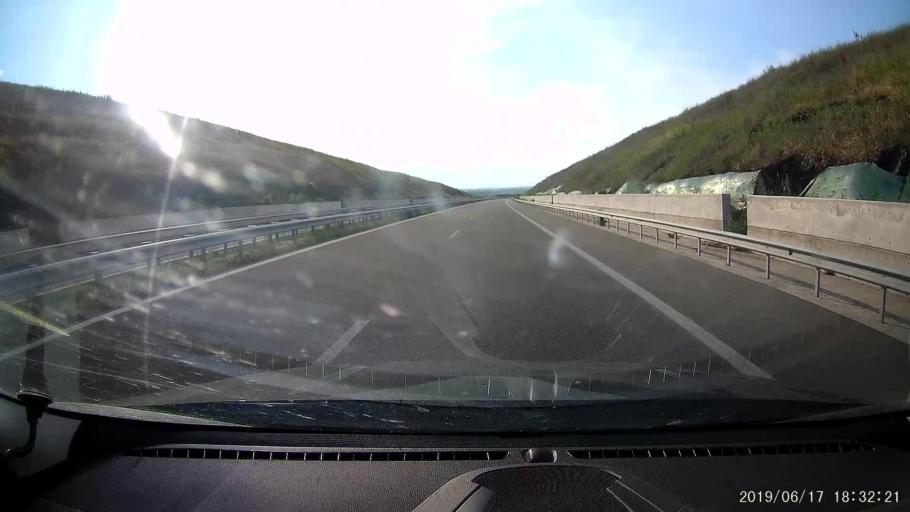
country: BG
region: Khaskovo
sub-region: Obshtina Dimitrovgrad
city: Dimitrovgrad
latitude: 42.0583
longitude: 25.4810
